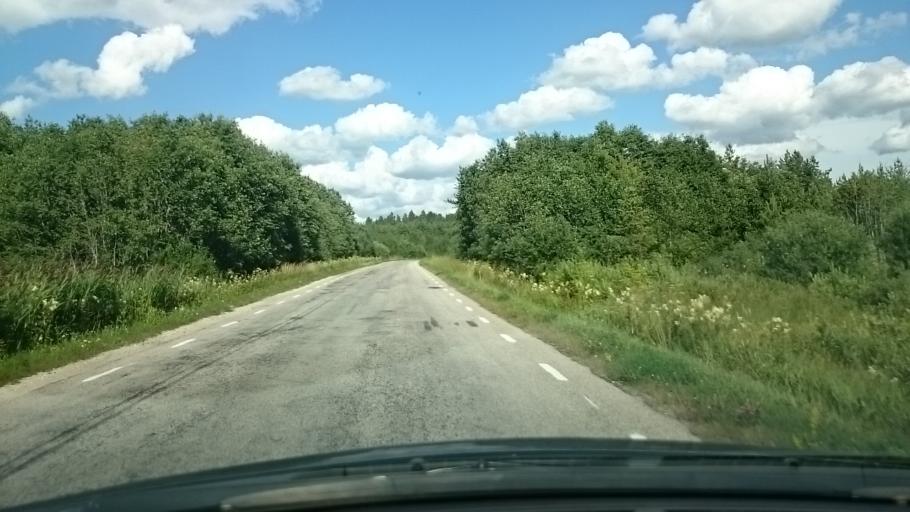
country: EE
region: Laeaene
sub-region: Haapsalu linn
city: Haapsalu
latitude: 59.0563
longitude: 23.5400
